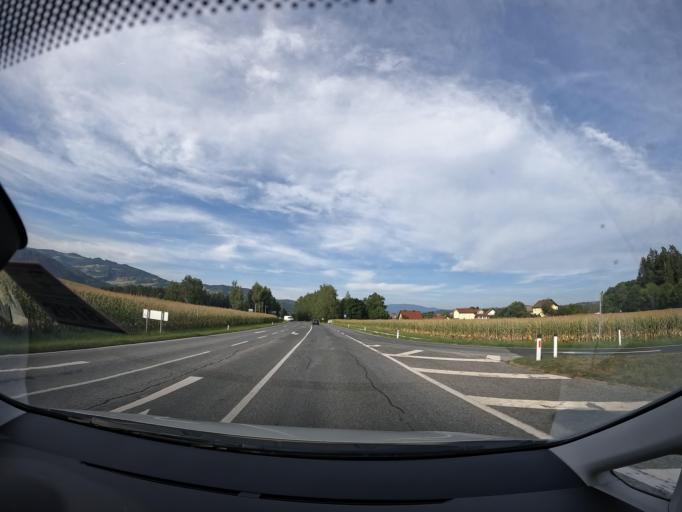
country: AT
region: Carinthia
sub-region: Politischer Bezirk Volkermarkt
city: Voelkermarkt
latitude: 46.6696
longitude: 14.6636
